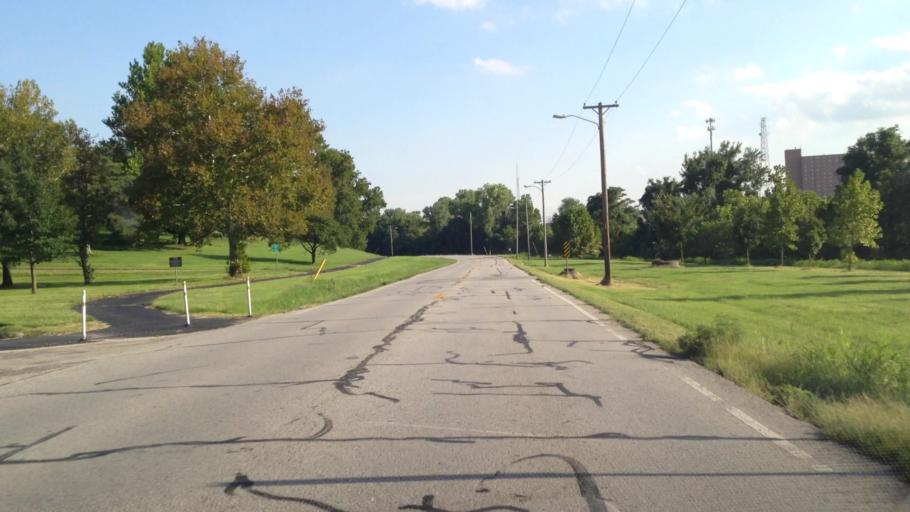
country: US
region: Missouri
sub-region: Jasper County
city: Joplin
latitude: 37.0956
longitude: -94.5108
